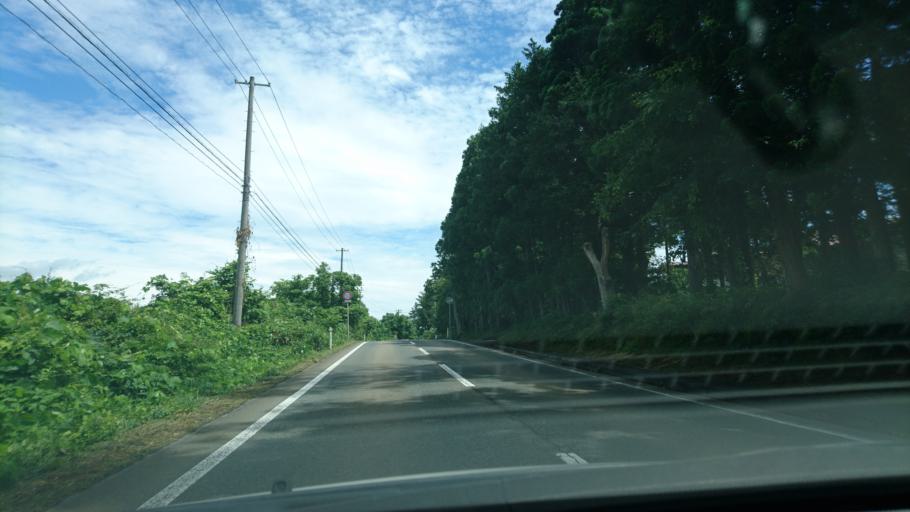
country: JP
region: Iwate
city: Hanamaki
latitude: 39.4156
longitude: 141.1730
